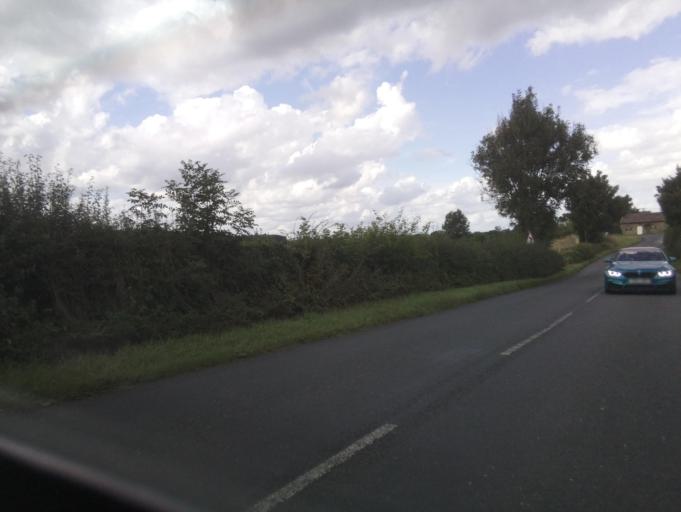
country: GB
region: England
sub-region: North Yorkshire
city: Bedale
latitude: 54.2460
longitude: -1.6910
